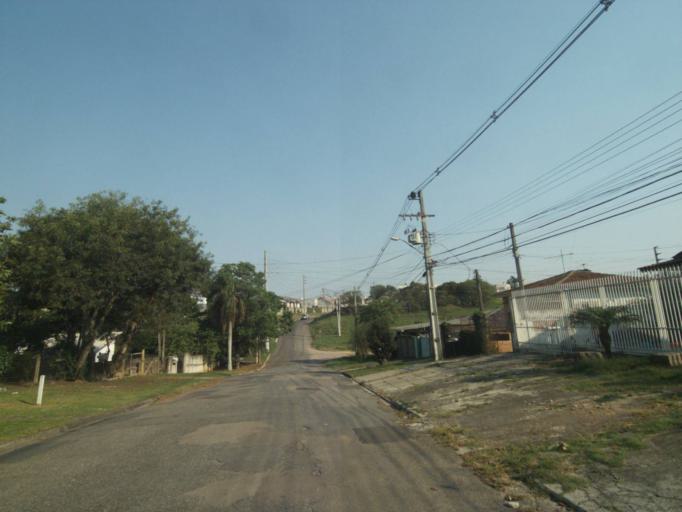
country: BR
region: Parana
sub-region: Curitiba
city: Curitiba
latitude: -25.4914
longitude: -49.2691
